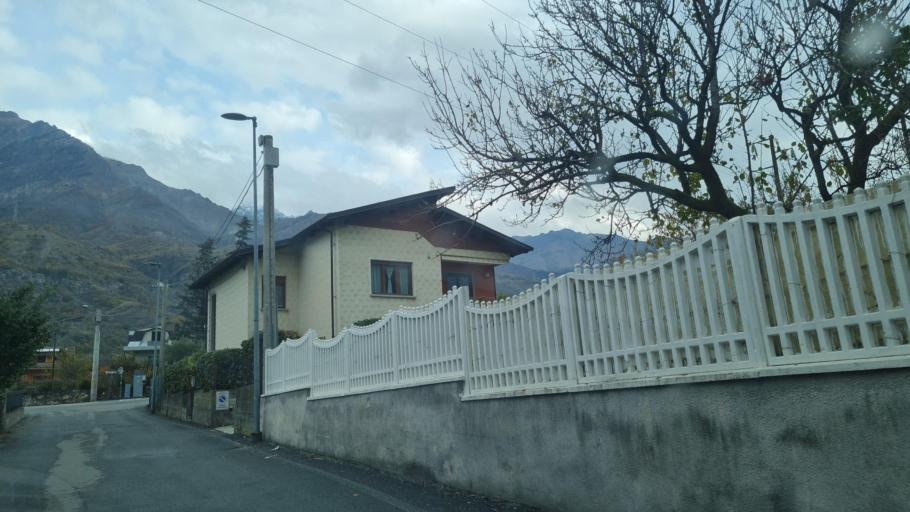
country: IT
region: Piedmont
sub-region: Provincia di Torino
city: Bussoleno
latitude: 45.1410
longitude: 7.1358
